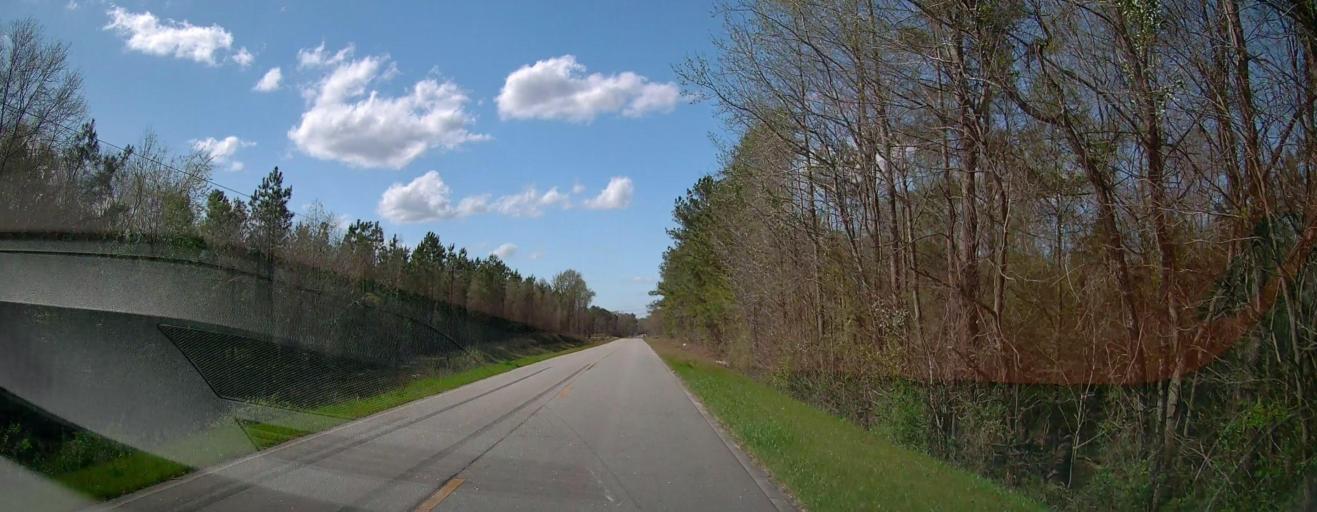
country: US
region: Georgia
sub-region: Wilkinson County
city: Gordon
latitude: 32.8392
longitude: -83.4389
